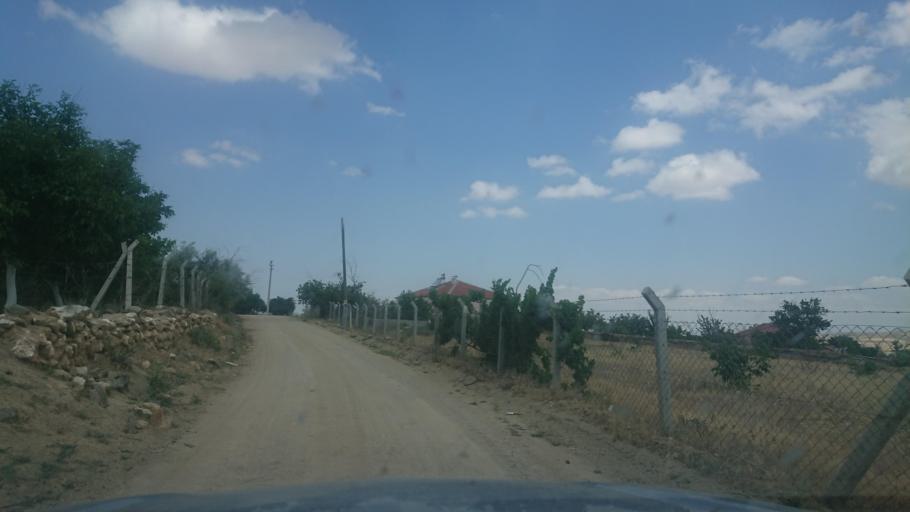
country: TR
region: Aksaray
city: Agacoren
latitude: 38.9340
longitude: 33.9525
